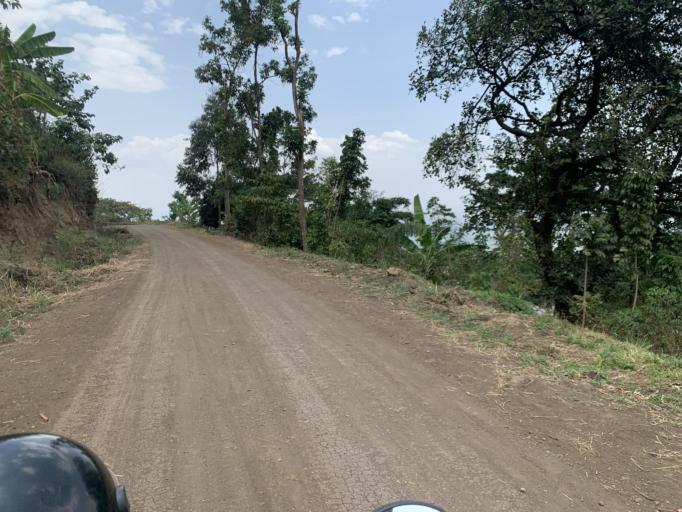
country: UG
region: Eastern Region
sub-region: Sironko District
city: Sironko
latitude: 1.2609
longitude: 34.3036
